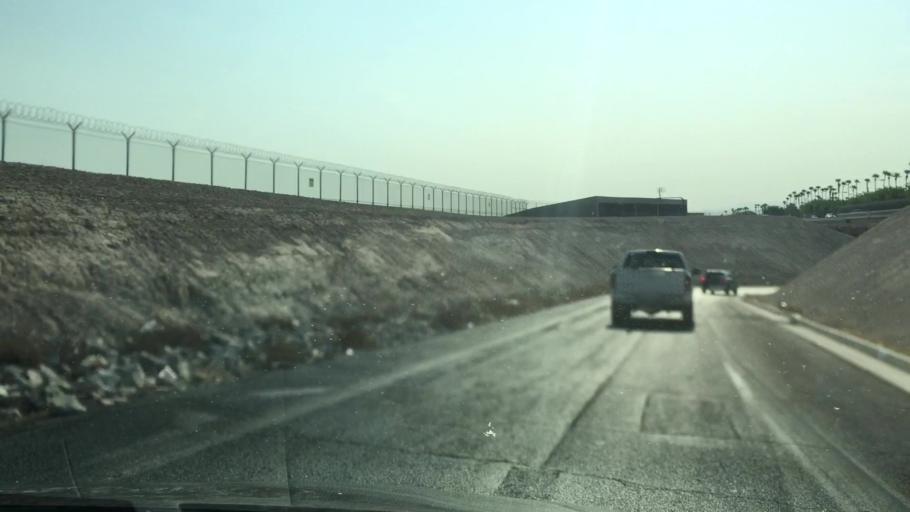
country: US
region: Nevada
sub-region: Clark County
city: Paradise
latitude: 36.0721
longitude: -115.1478
